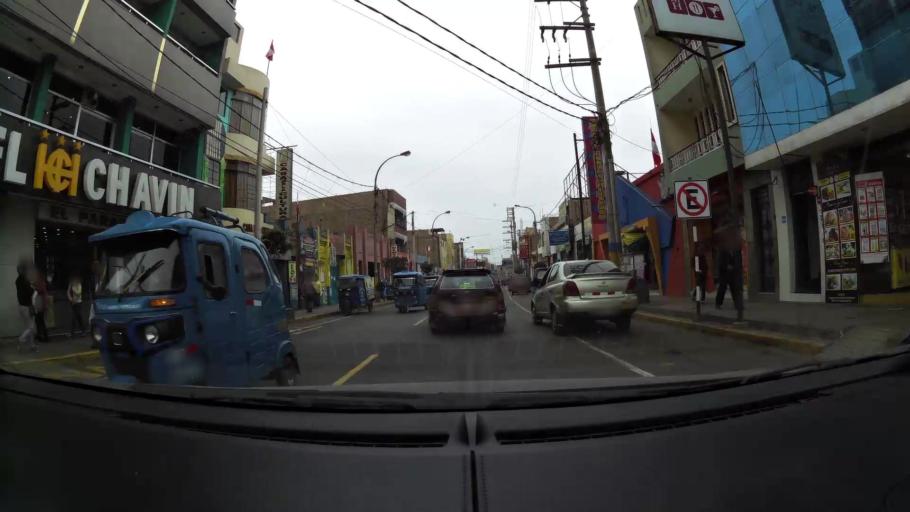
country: PE
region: Lima
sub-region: Barranca
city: Barranca
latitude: -10.7522
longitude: -77.7602
